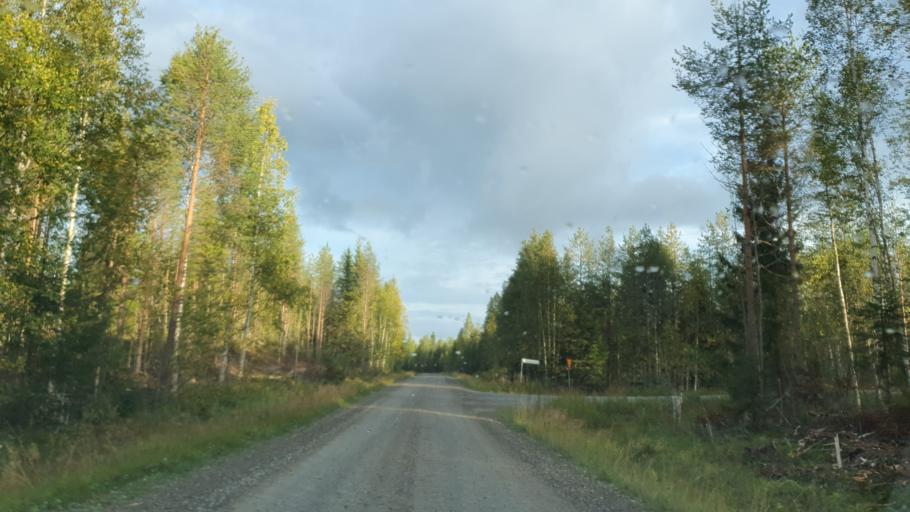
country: FI
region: Kainuu
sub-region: Kehys-Kainuu
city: Kuhmo
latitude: 64.4215
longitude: 29.3628
